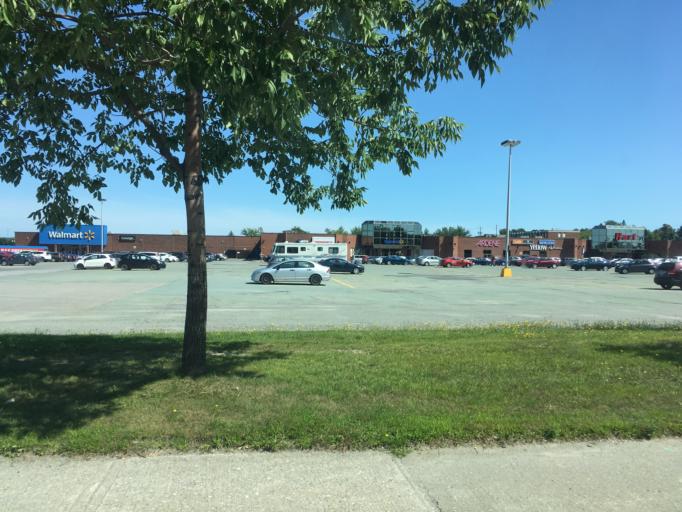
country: CA
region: Quebec
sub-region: Estrie
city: Sherbrooke
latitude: 45.4217
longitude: -71.8729
